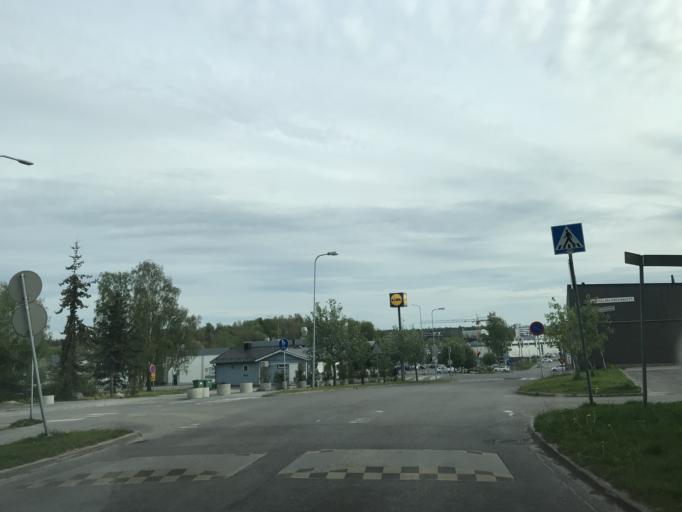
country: FI
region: Varsinais-Suomi
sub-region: Turku
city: Turku
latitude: 60.4509
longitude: 22.3089
